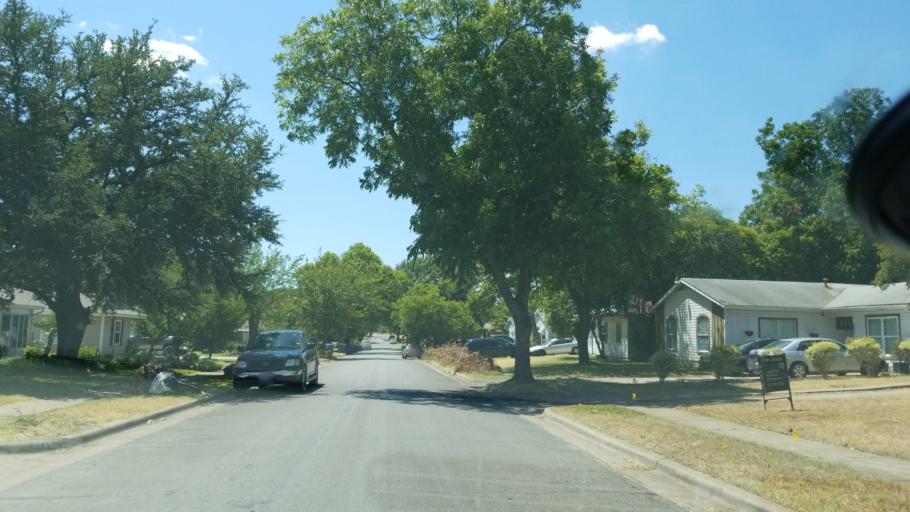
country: US
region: Texas
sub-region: Dallas County
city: Cockrell Hill
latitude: 32.7235
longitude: -96.8832
